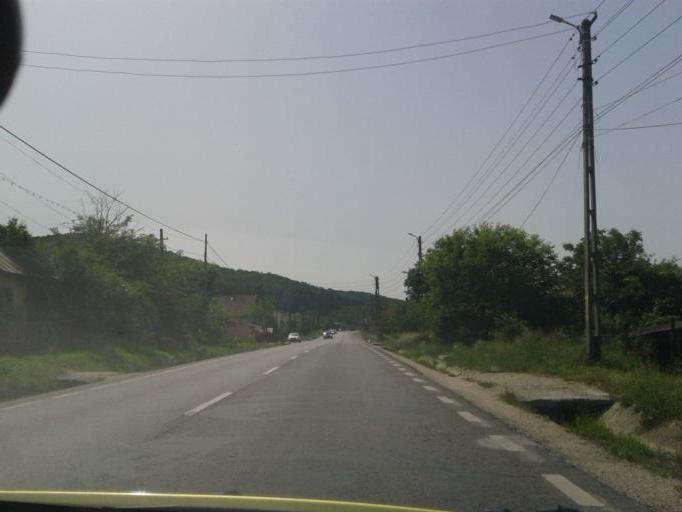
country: RO
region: Arges
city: Draganu-Olteni
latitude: 44.9243
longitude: 24.7175
